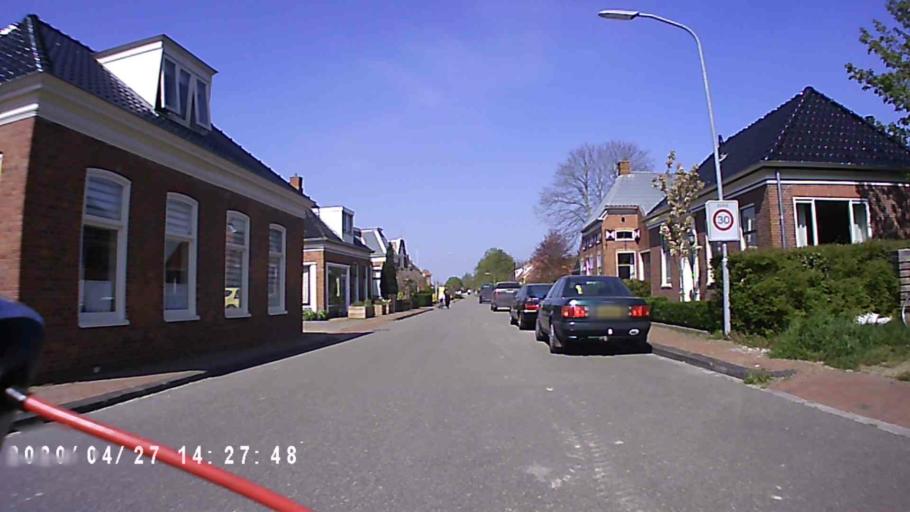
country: NL
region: Groningen
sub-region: Gemeente De Marne
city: Ulrum
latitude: 53.3877
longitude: 6.3927
